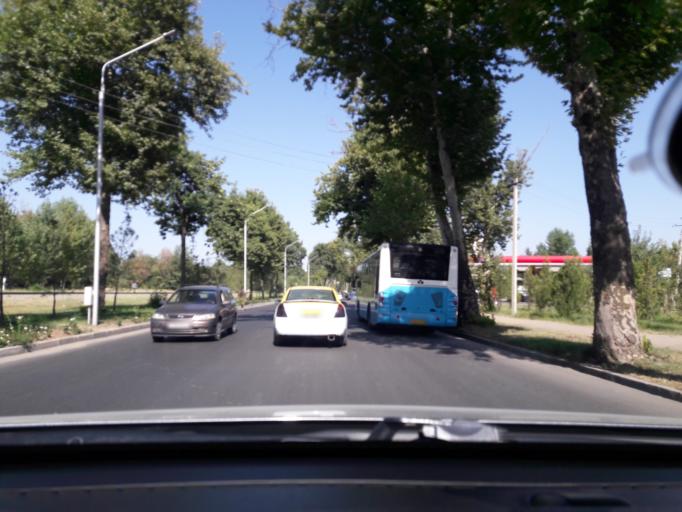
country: TJ
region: Dushanbe
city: Dushanbe
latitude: 38.5694
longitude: 68.7605
